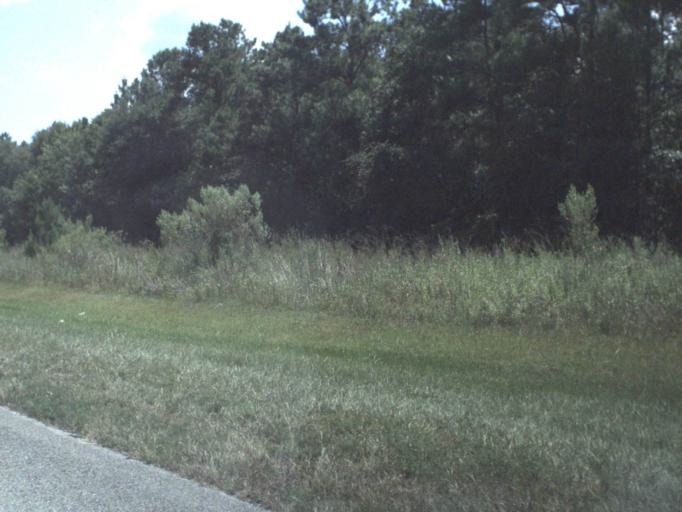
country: US
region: Florida
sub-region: Alachua County
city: Hawthorne
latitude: 29.6432
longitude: -82.1075
